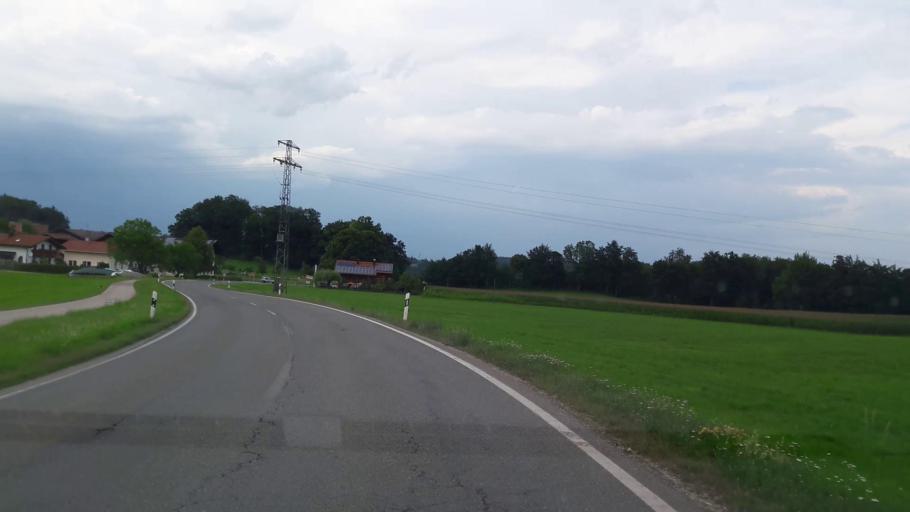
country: DE
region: Bavaria
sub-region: Upper Bavaria
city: Bergen
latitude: 47.8321
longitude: 12.5952
